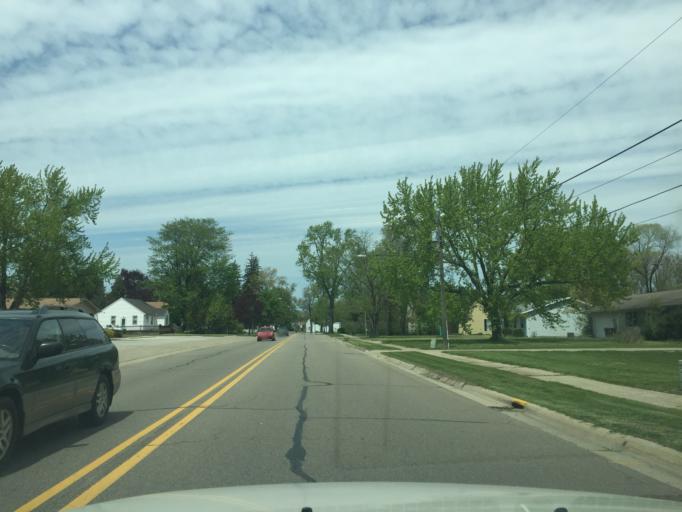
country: US
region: Michigan
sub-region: Berrien County
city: Stevensville
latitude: 42.0097
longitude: -86.5191
